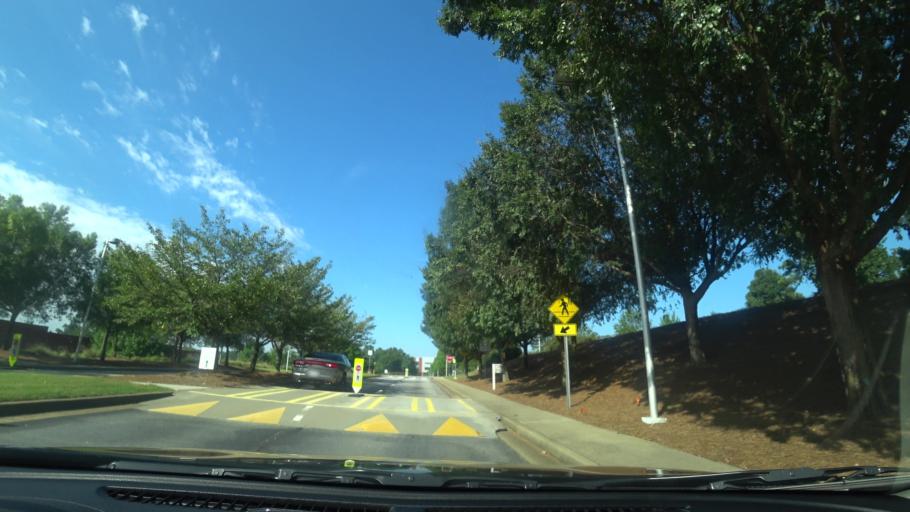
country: US
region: Georgia
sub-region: Gwinnett County
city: Lawrenceville
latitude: 33.9808
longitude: -84.0014
